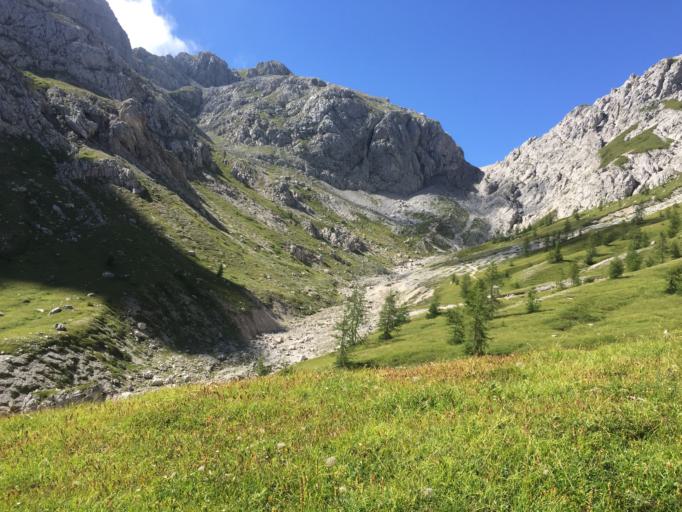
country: IT
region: Veneto
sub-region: Provincia di Belluno
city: Granvilla
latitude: 46.5459
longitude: 12.7294
